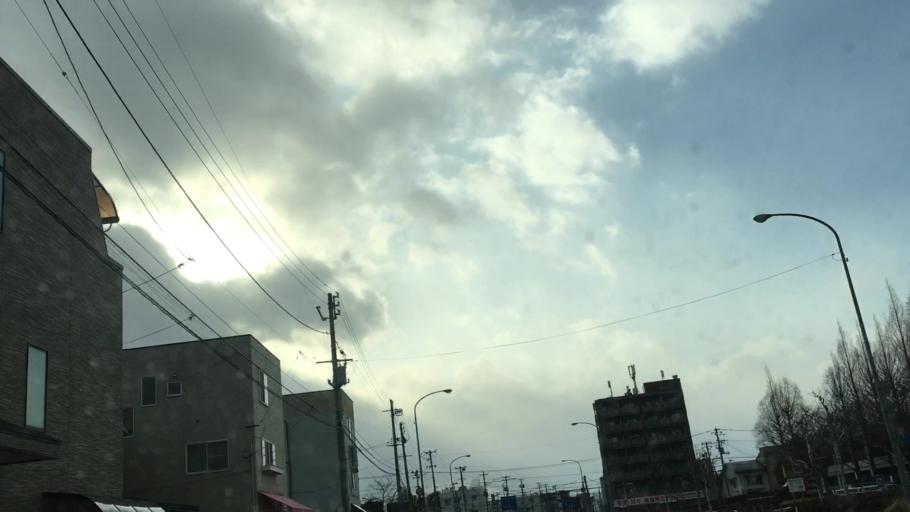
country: JP
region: Iwate
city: Morioka-shi
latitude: 39.7127
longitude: 141.1460
